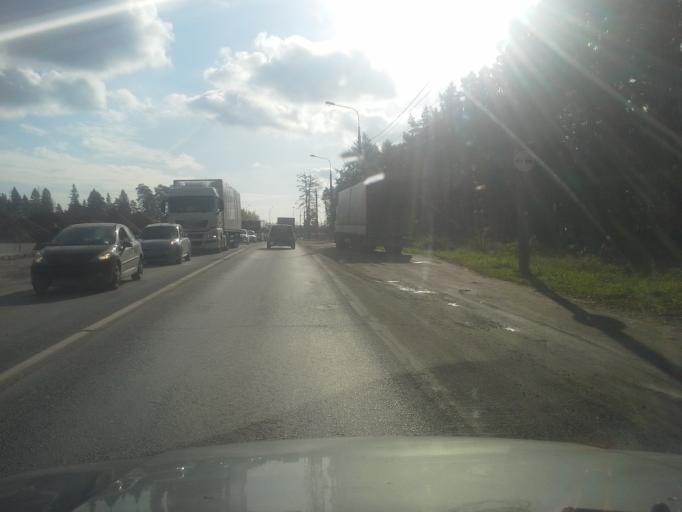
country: RU
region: Moskovskaya
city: Zvenigorod
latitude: 55.7040
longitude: 36.8788
